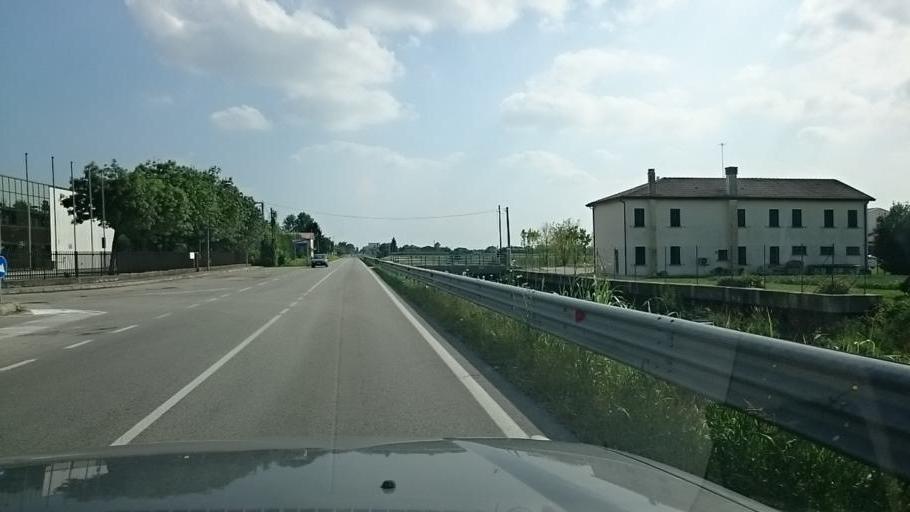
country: IT
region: Veneto
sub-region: Provincia di Padova
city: Cavino
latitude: 45.5308
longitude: 11.8706
